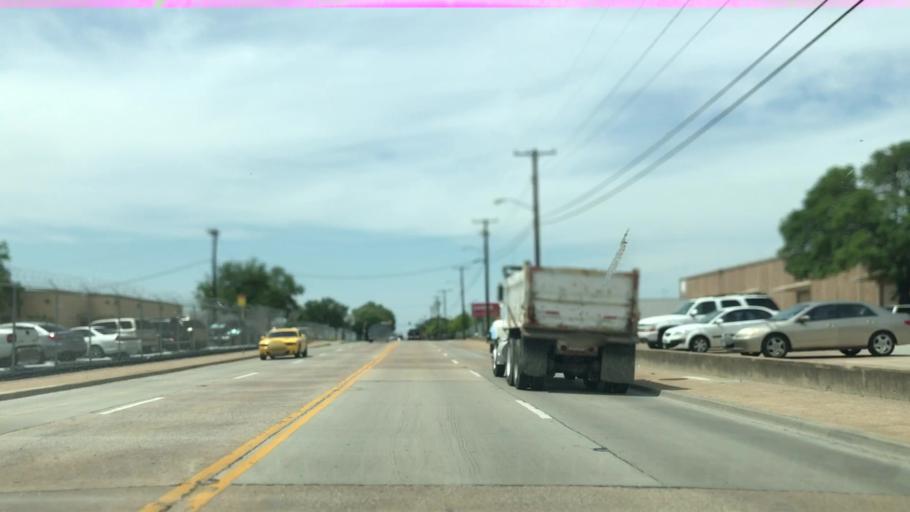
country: US
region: Texas
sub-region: Dallas County
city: University Park
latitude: 32.8285
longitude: -96.8344
